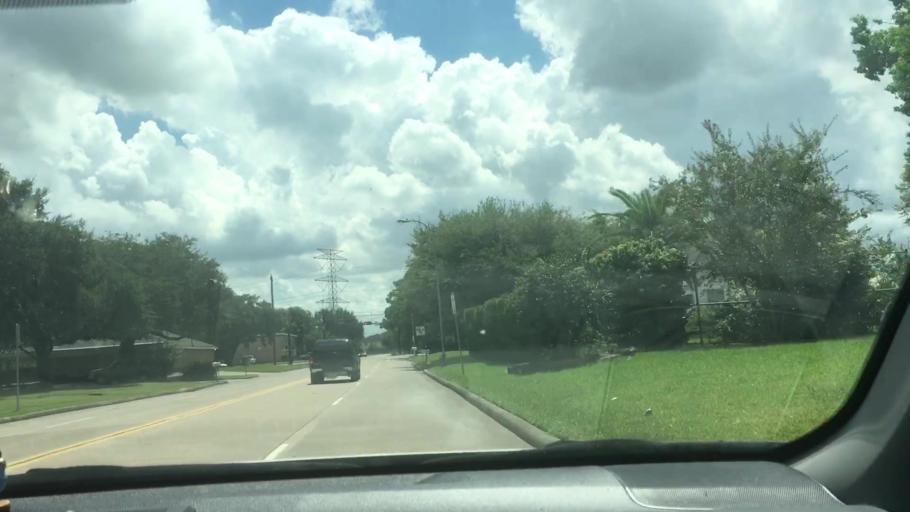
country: US
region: Texas
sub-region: Fort Bend County
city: Missouri City
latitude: 29.6113
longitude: -95.5443
